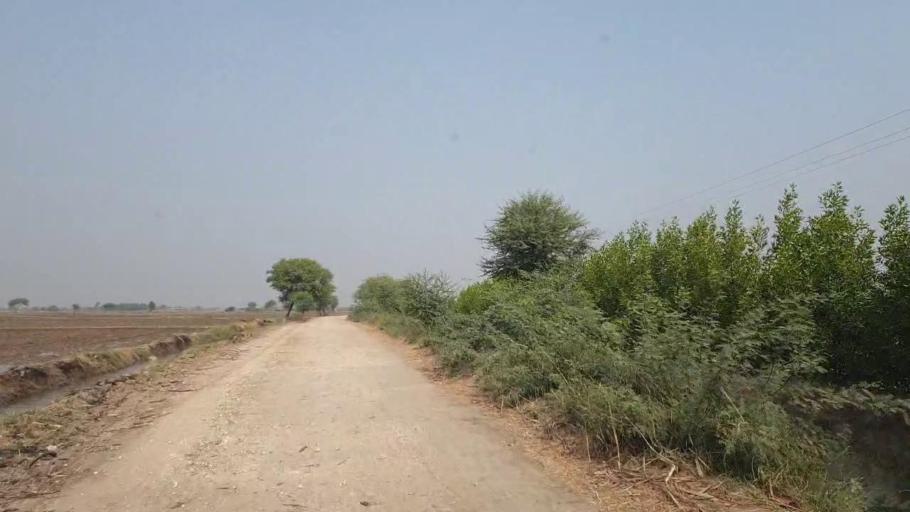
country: PK
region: Sindh
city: Matli
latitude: 25.1460
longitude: 68.7294
